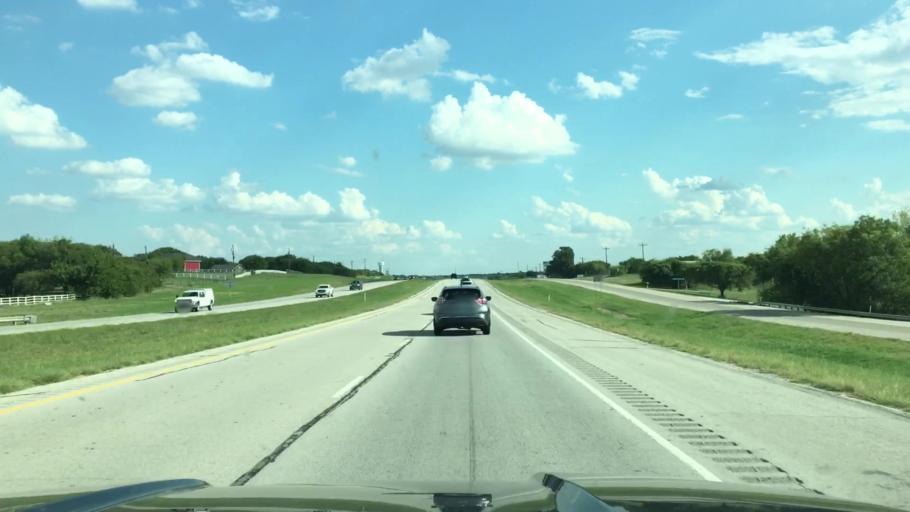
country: US
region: Texas
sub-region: Tarrant County
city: Pecan Acres
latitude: 32.9892
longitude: -97.4297
